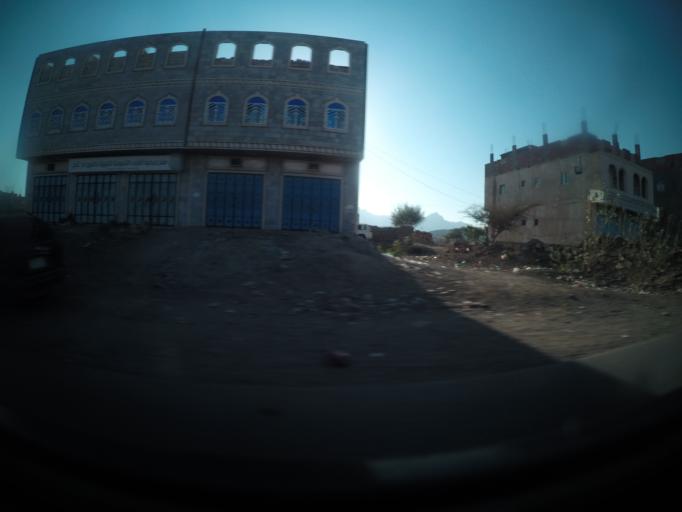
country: YE
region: Lahij
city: Habil ar Raydah
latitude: 13.6395
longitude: 44.8590
